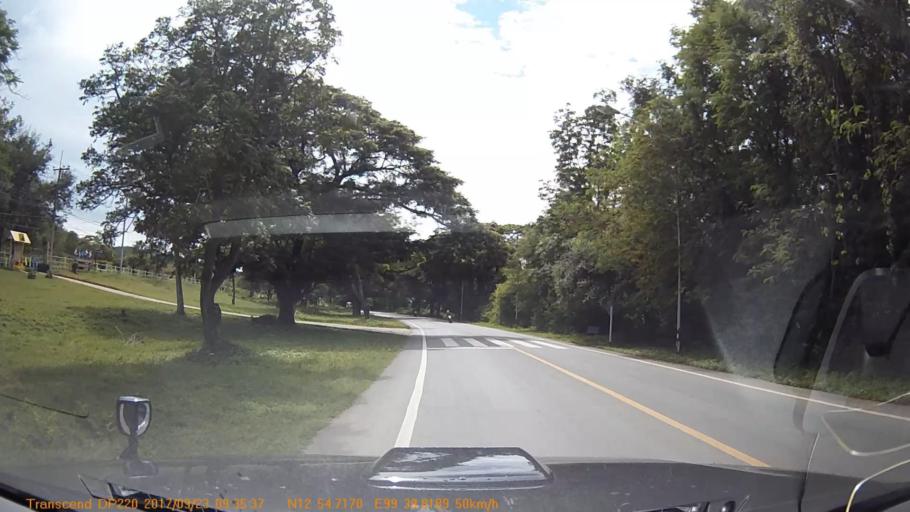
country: TH
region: Phetchaburi
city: Kaeng Krachan
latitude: 12.9120
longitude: 99.6634
